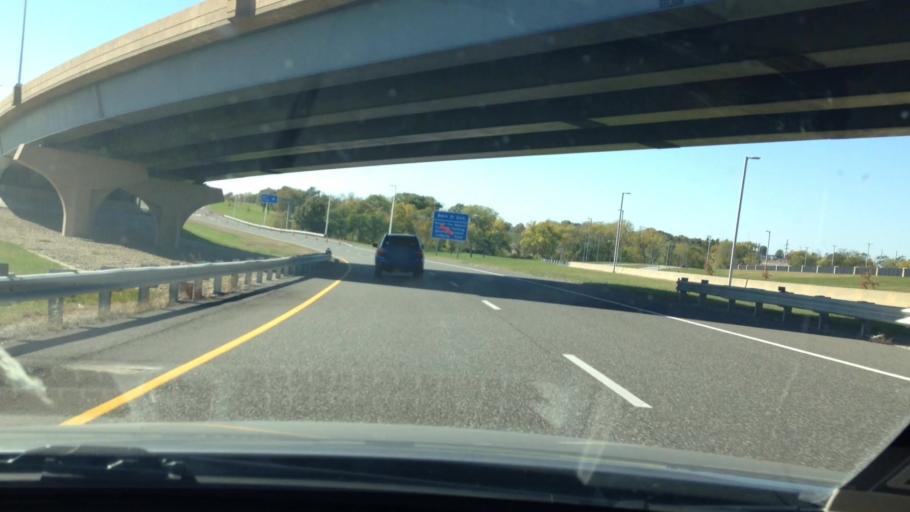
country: US
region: Missouri
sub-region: Platte County
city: Weatherby Lake
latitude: 39.3112
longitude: -94.7018
